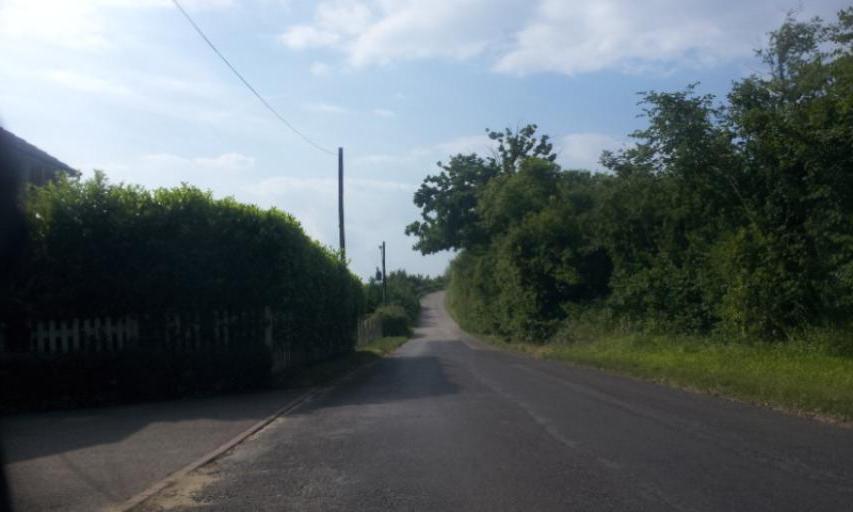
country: GB
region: England
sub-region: Kent
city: Lenham
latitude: 51.2293
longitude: 0.6940
